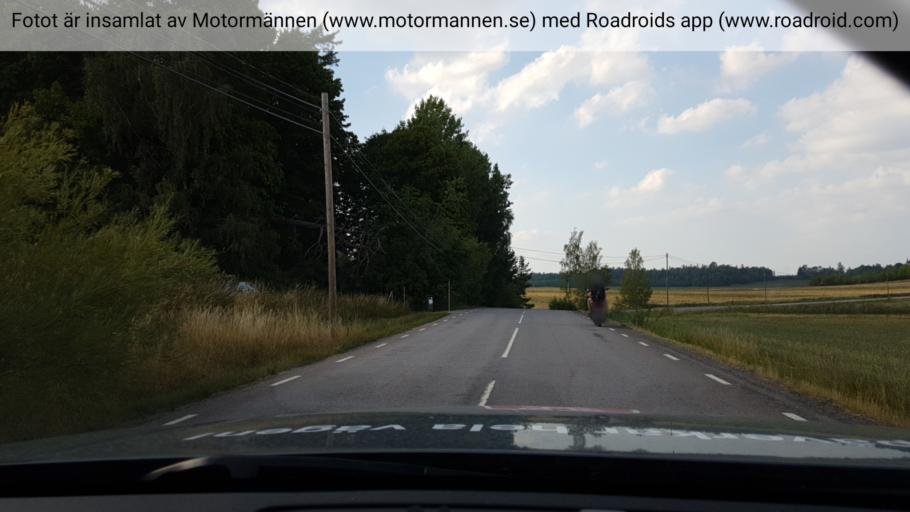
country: SE
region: Soedermanland
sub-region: Gnesta Kommun
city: Gnesta
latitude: 59.0666
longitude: 17.2949
